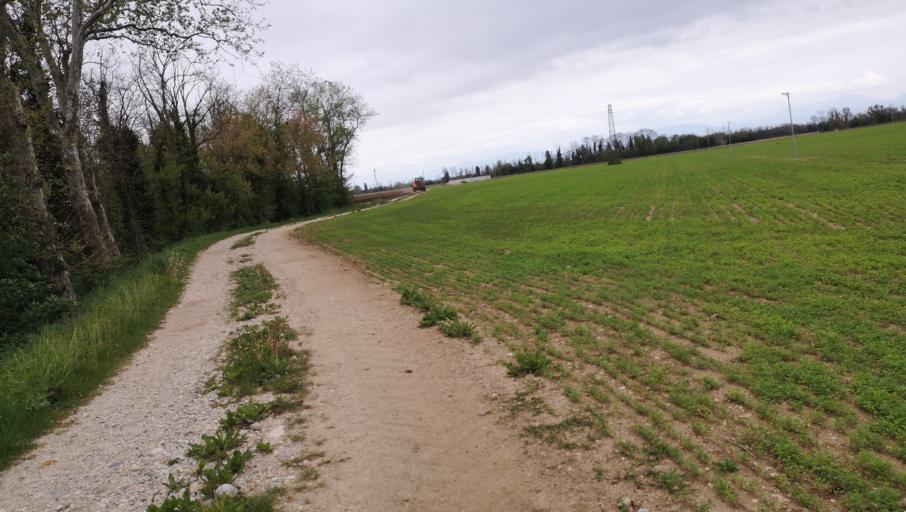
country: IT
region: Friuli Venezia Giulia
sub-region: Provincia di Udine
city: Basiliano-Vissandone
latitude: 46.0075
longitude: 13.0886
